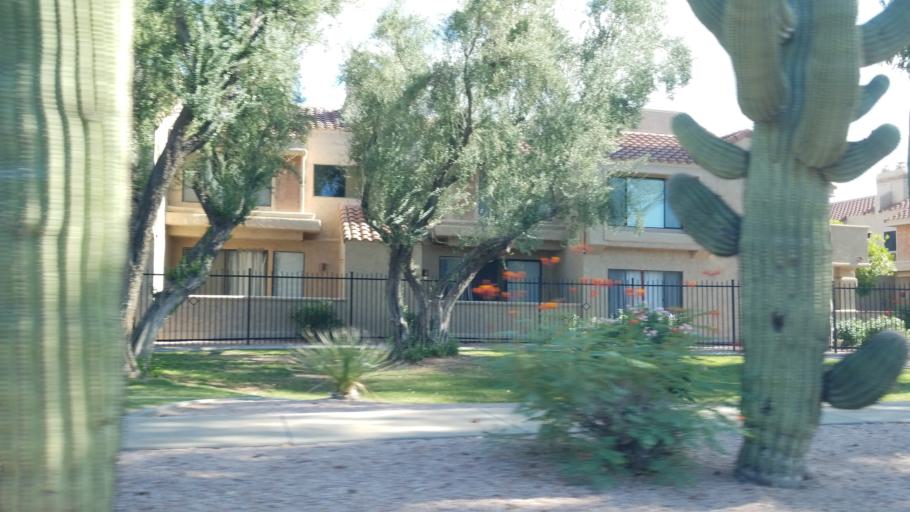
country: US
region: Arizona
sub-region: Maricopa County
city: Scottsdale
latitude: 33.5737
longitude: -111.8653
